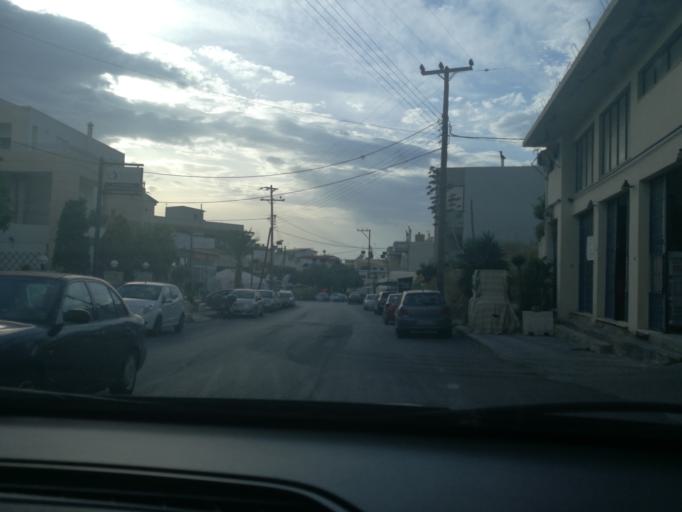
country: GR
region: Crete
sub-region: Nomos Irakleiou
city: Irakleion
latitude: 35.3169
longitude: 25.1368
